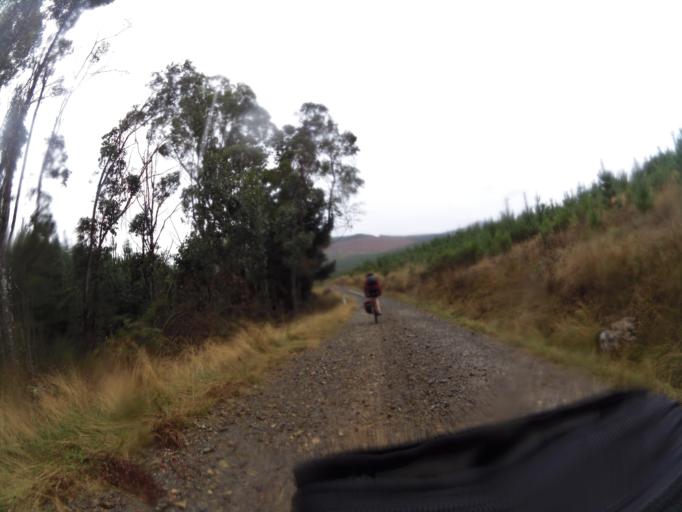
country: AU
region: New South Wales
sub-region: Greater Hume Shire
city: Holbrook
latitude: -36.2147
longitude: 147.5667
